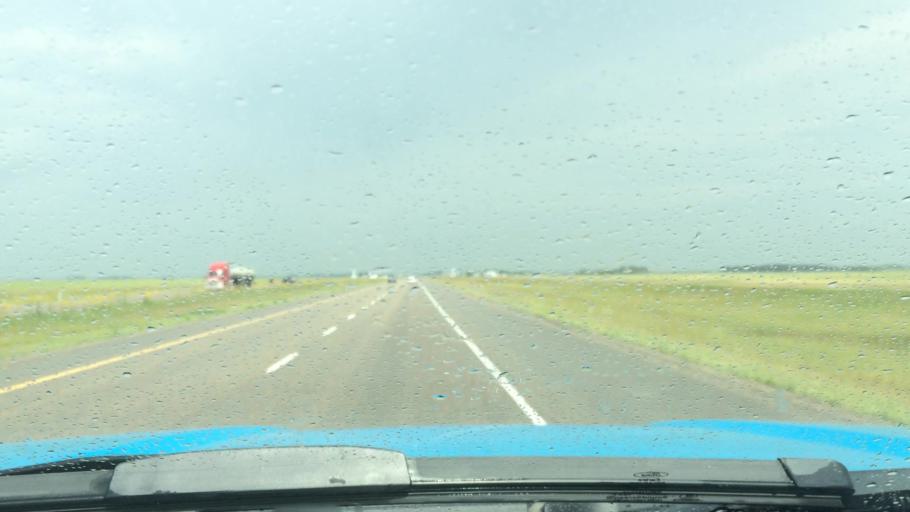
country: CA
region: Alberta
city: Didsbury
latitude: 51.6885
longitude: -114.0252
